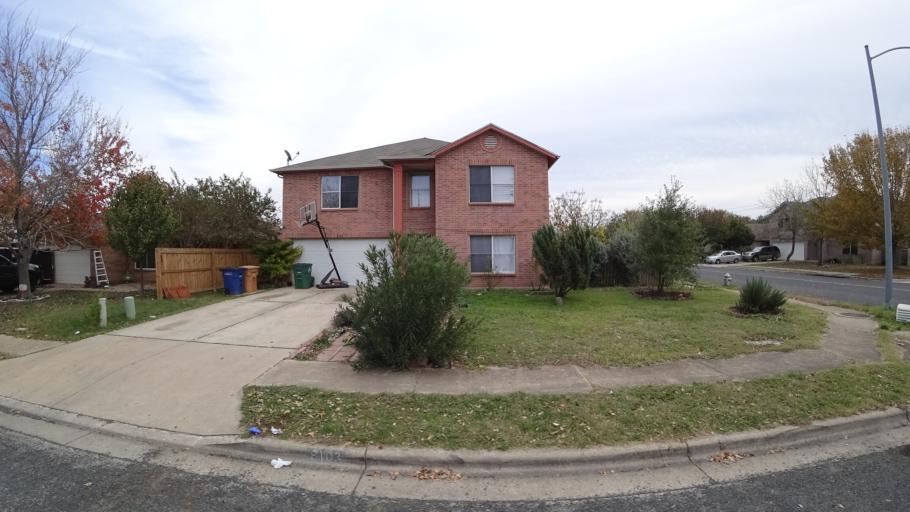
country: US
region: Texas
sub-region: Travis County
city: Onion Creek
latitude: 30.1573
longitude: -97.7405
